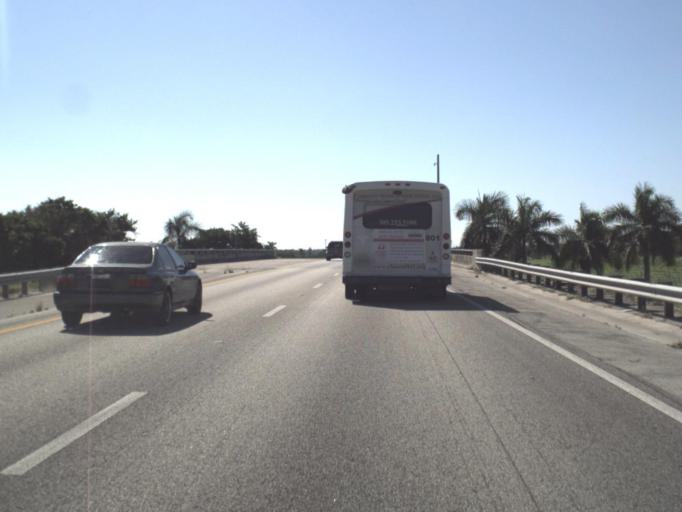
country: US
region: Florida
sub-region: Miami-Dade County
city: Goulds
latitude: 25.5603
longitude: -80.3631
